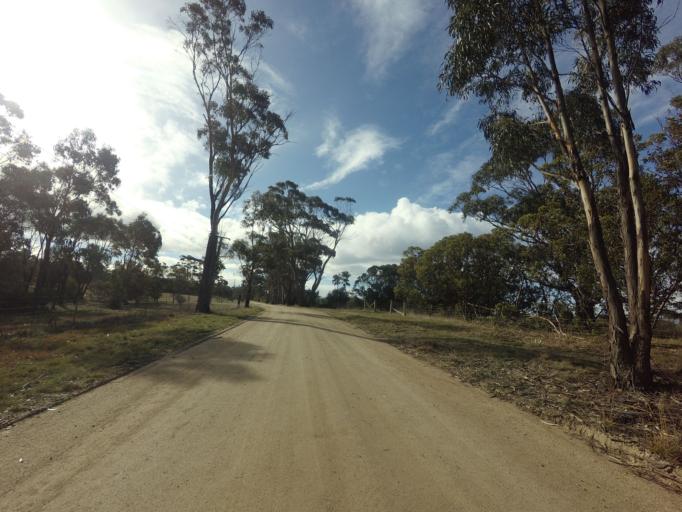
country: AU
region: Tasmania
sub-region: Sorell
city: Sorell
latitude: -42.3073
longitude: 147.9965
